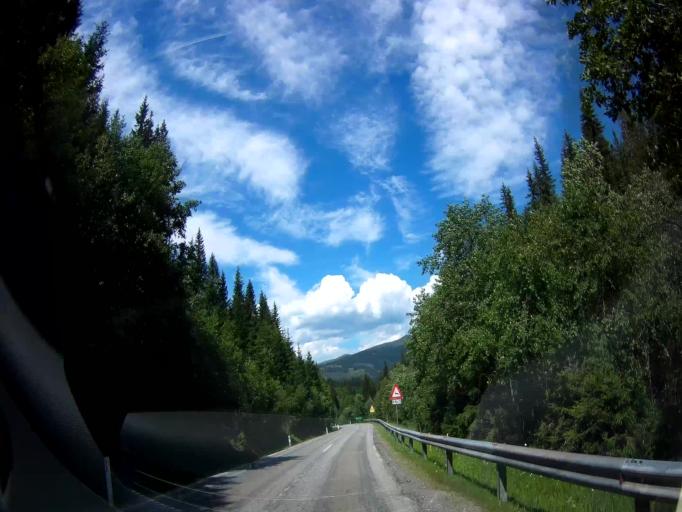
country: AT
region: Styria
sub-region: Politischer Bezirk Murau
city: Stadl an der Mur
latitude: 46.9792
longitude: 14.0064
